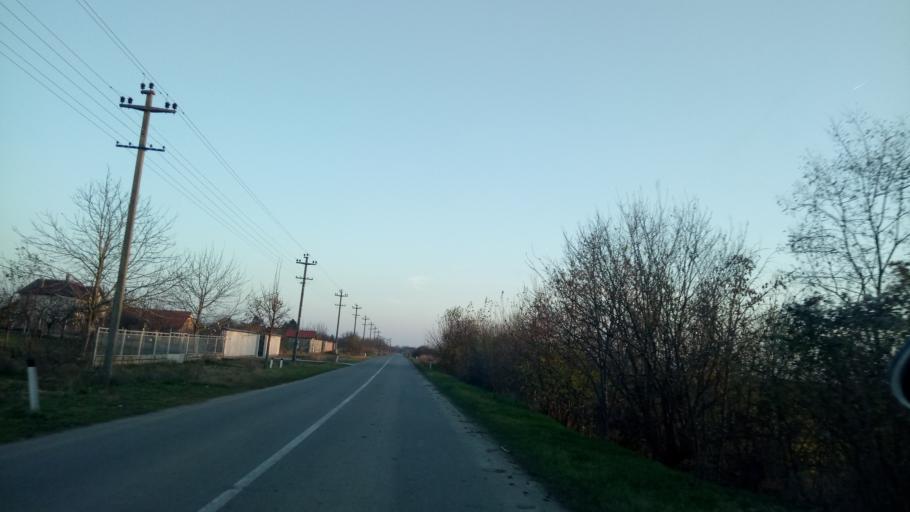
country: RS
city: Surduk
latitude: 45.0910
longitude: 20.2995
